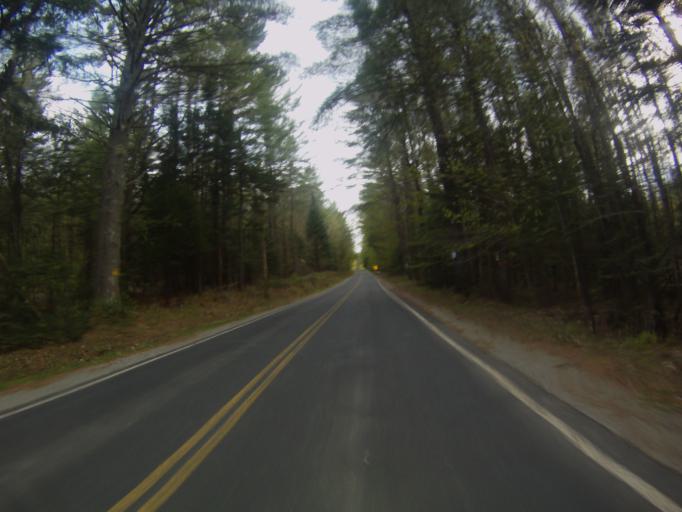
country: US
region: New York
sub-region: Warren County
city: Warrensburg
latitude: 43.8136
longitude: -73.9355
